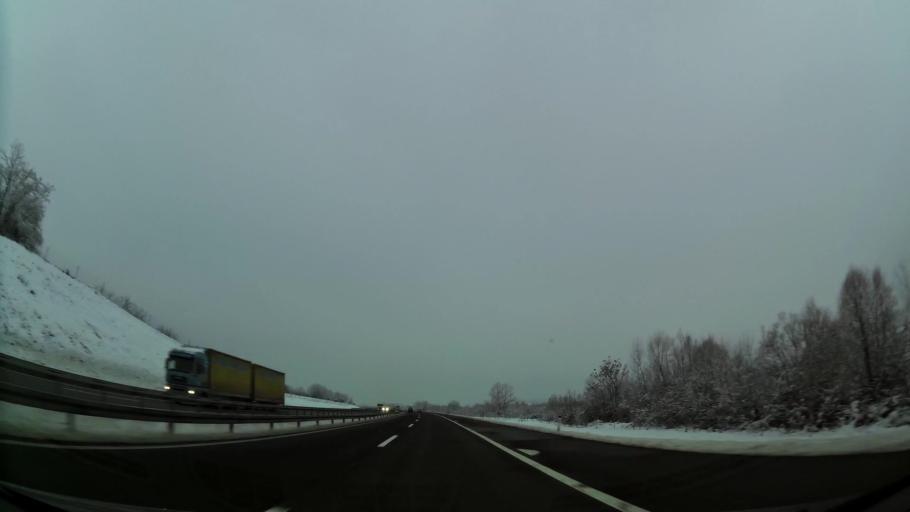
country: RS
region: Central Serbia
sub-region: Belgrade
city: Grocka
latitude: 44.5798
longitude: 20.7819
